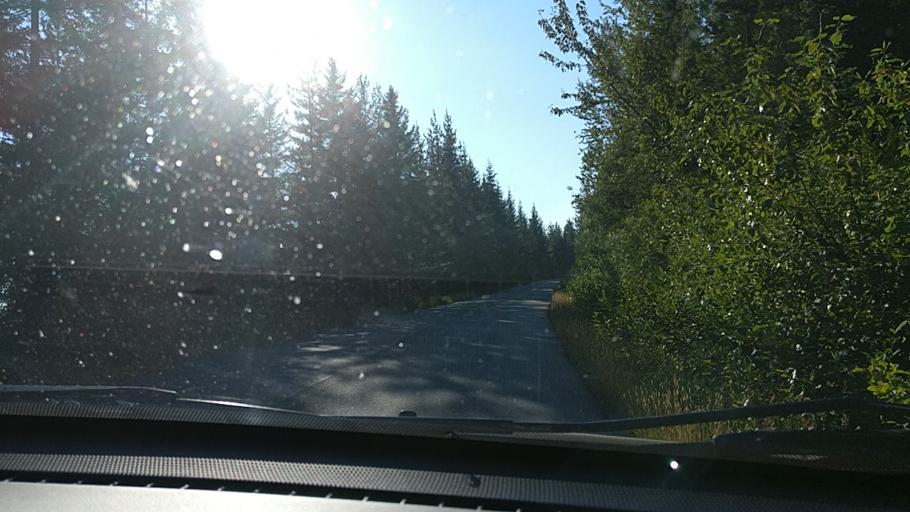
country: CA
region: British Columbia
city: Revelstoke
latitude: 51.0076
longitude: -118.1733
